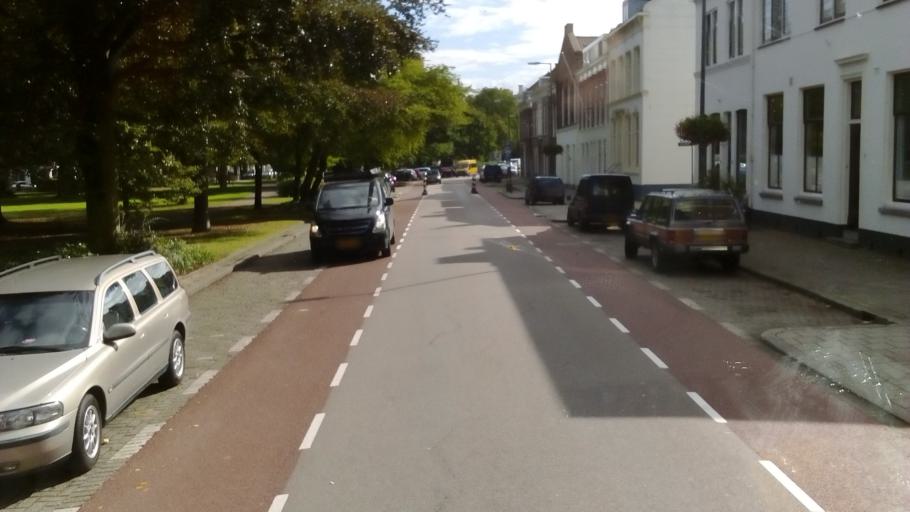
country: NL
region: South Holland
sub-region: Gemeente Schiedam
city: Schiedam
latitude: 51.9112
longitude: 4.4037
